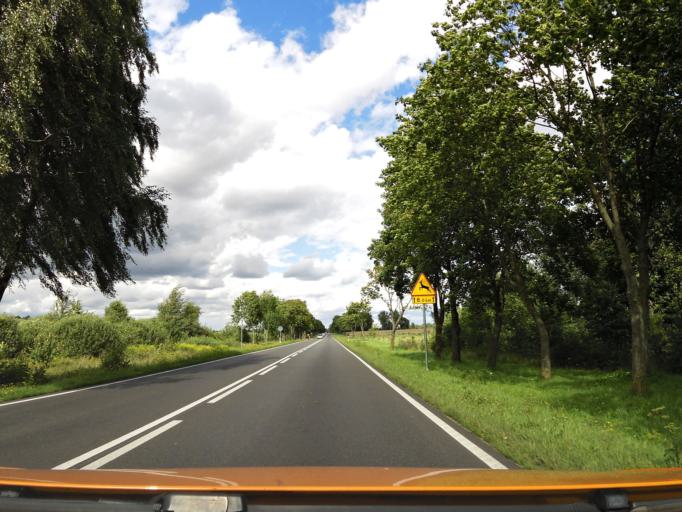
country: PL
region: West Pomeranian Voivodeship
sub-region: Powiat goleniowski
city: Nowogard
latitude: 53.7270
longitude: 15.1985
